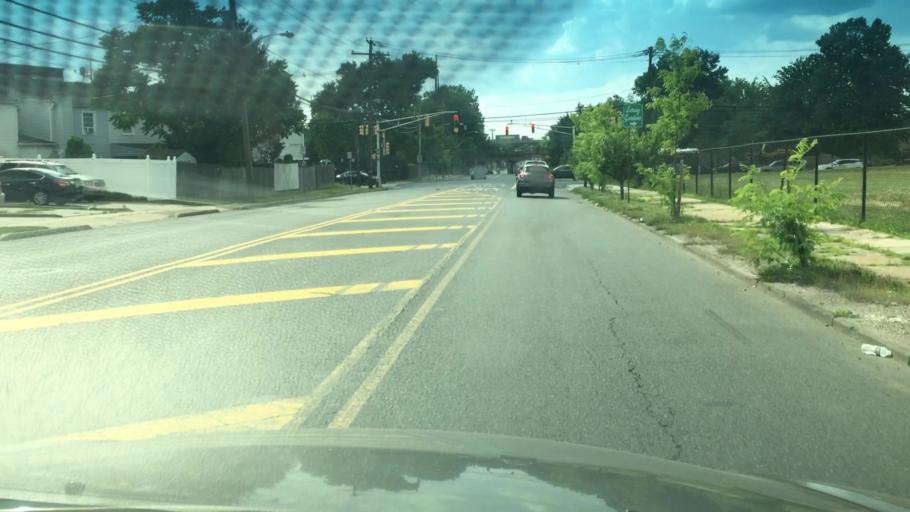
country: US
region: New Jersey
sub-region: Union County
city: Elizabeth
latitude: 40.6565
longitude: -74.1815
